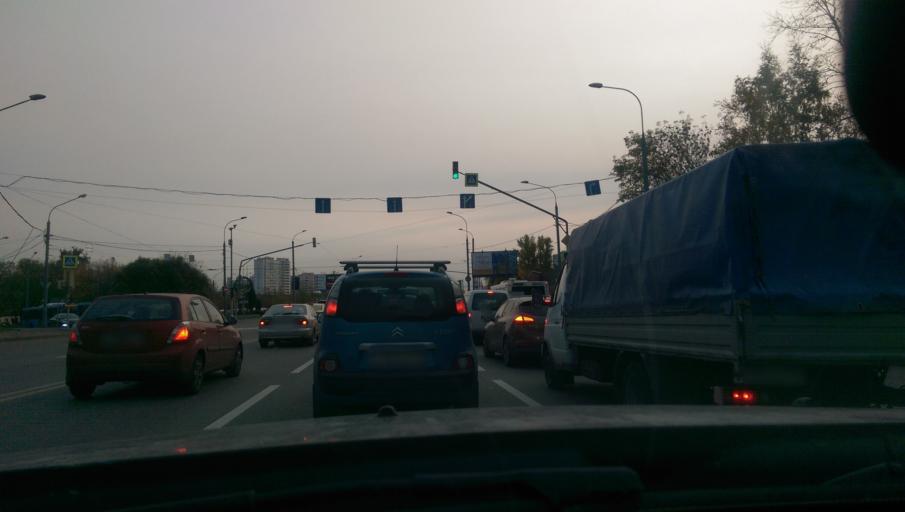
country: RU
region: Moscow
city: Vatutino
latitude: 55.8883
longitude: 37.6741
